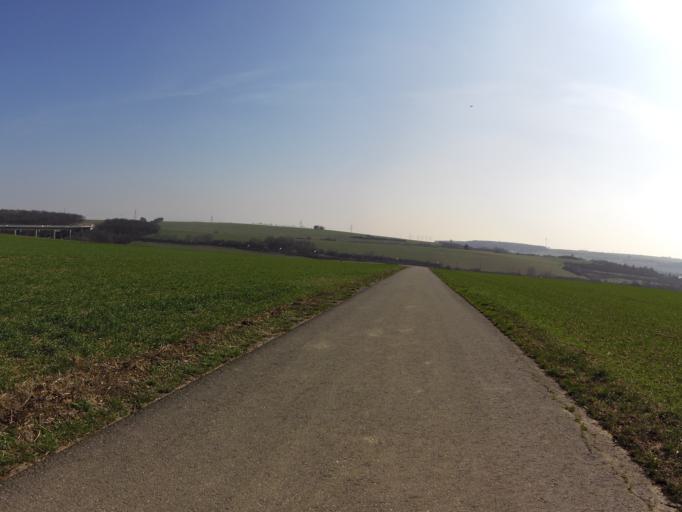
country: DE
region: Bavaria
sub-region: Regierungsbezirk Unterfranken
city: Rottendorf
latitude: 49.8068
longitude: 10.0370
